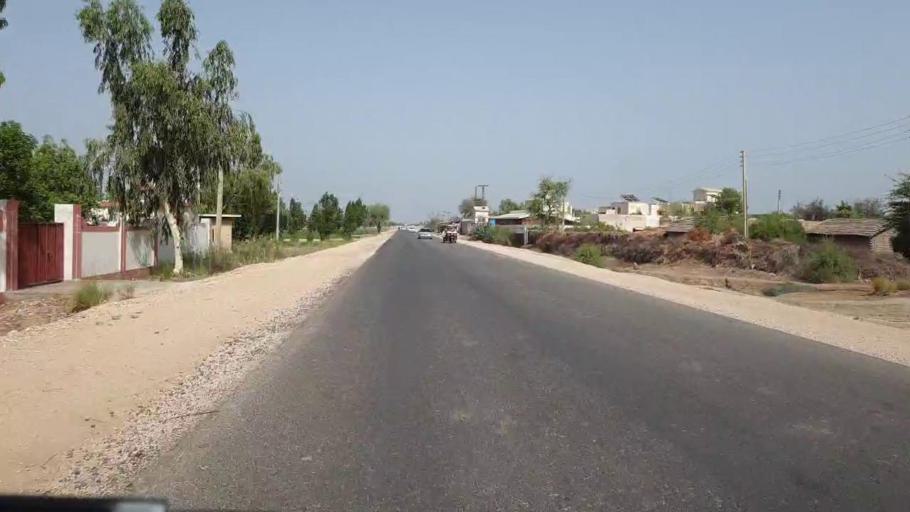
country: PK
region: Sindh
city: Sakrand
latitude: 26.2638
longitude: 68.1777
